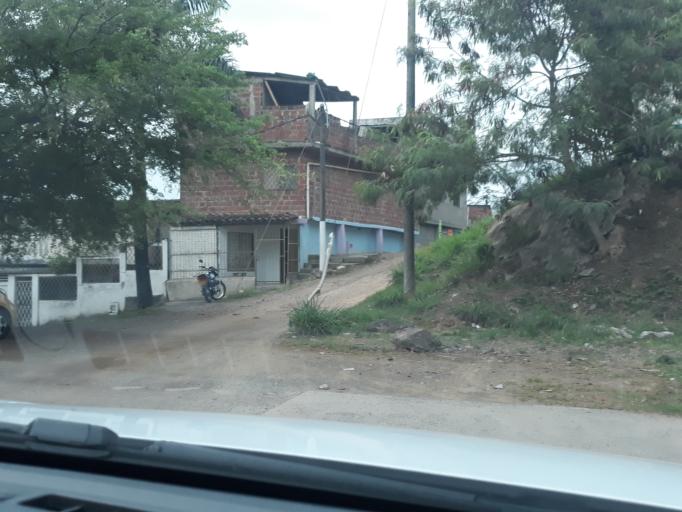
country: CO
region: Valle del Cauca
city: Cali
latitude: 3.4288
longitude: -76.5528
